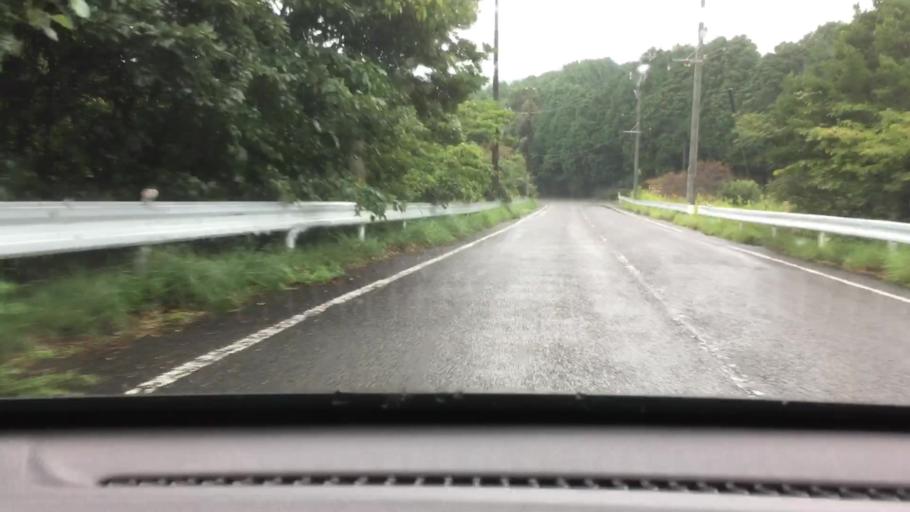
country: JP
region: Nagasaki
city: Togitsu
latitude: 32.8786
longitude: 129.7606
